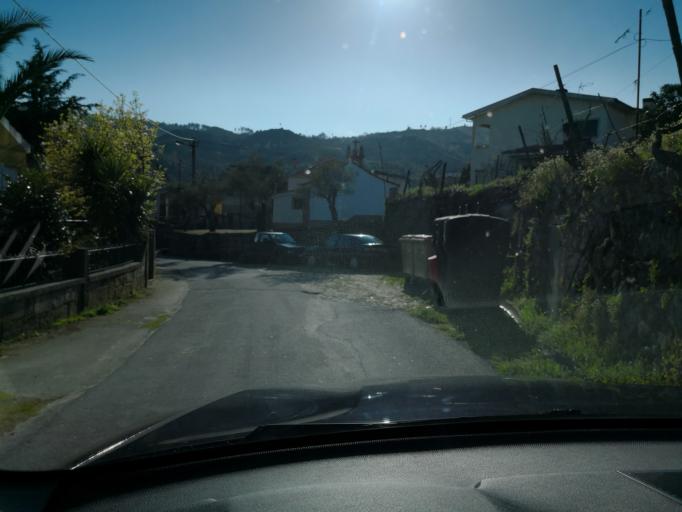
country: PT
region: Vila Real
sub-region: Vila Real
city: Vila Real
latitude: 41.2866
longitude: -7.7878
